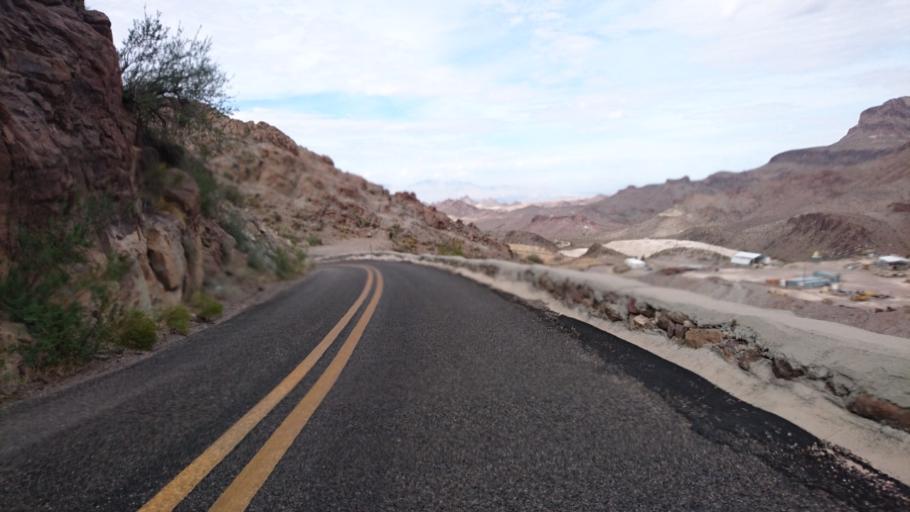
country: US
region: Arizona
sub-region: Mohave County
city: Bullhead City
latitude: 35.0423
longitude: -114.3750
